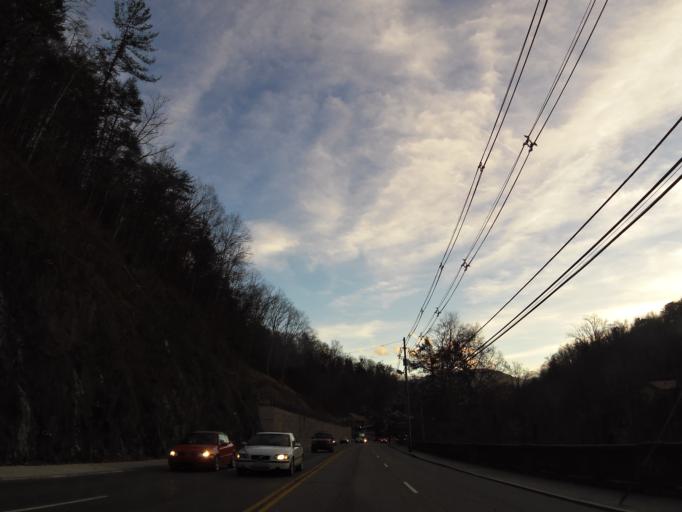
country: US
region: Tennessee
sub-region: Sevier County
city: Gatlinburg
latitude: 35.7227
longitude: -83.5100
